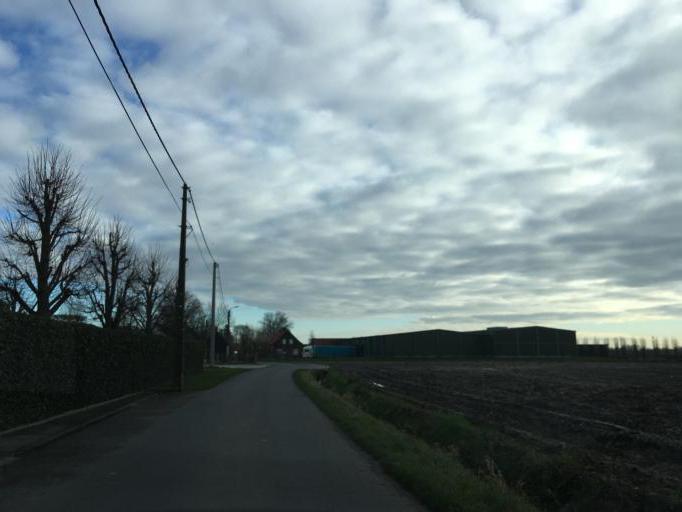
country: BE
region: Flanders
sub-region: Provincie West-Vlaanderen
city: Roeselare
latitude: 50.9091
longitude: 3.1191
